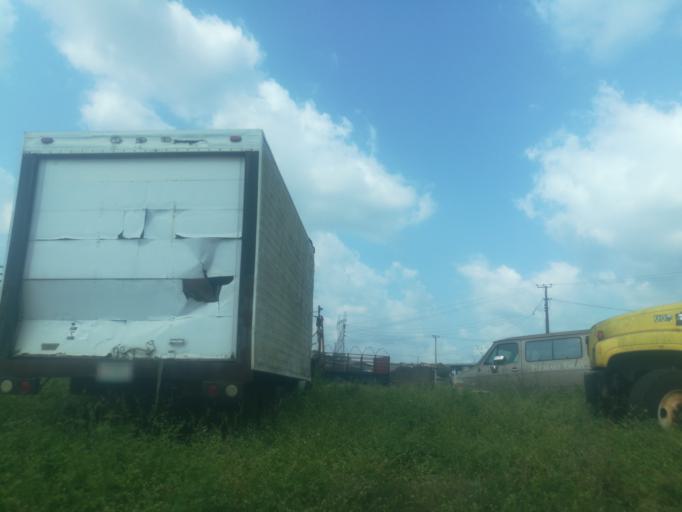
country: NG
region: Oyo
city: Moniya
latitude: 7.5170
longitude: 3.9142
